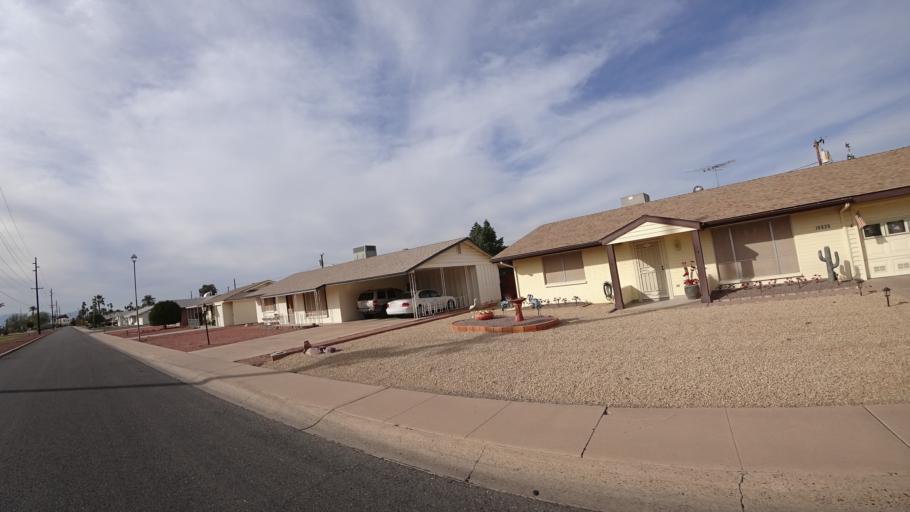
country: US
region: Arizona
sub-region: Maricopa County
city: Youngtown
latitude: 33.5948
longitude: -112.2934
